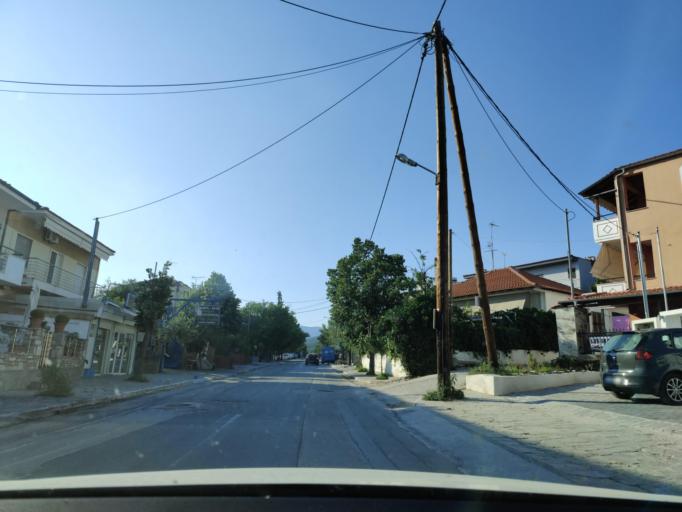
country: GR
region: East Macedonia and Thrace
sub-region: Nomos Kavalas
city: Limenaria
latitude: 40.6123
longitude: 24.6063
